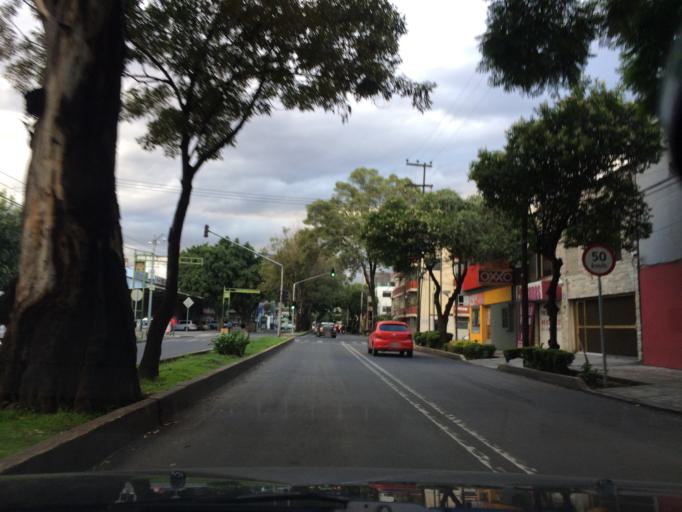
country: MX
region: Mexico City
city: Coyoacan
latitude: 19.3661
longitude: -99.1537
